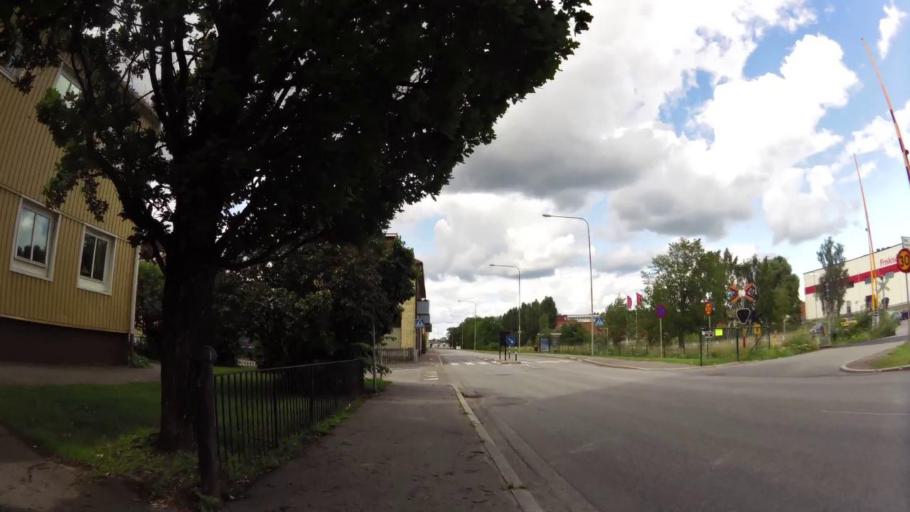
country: SE
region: OEstergoetland
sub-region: Linkopings Kommun
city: Linkoping
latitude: 58.4083
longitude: 15.6467
